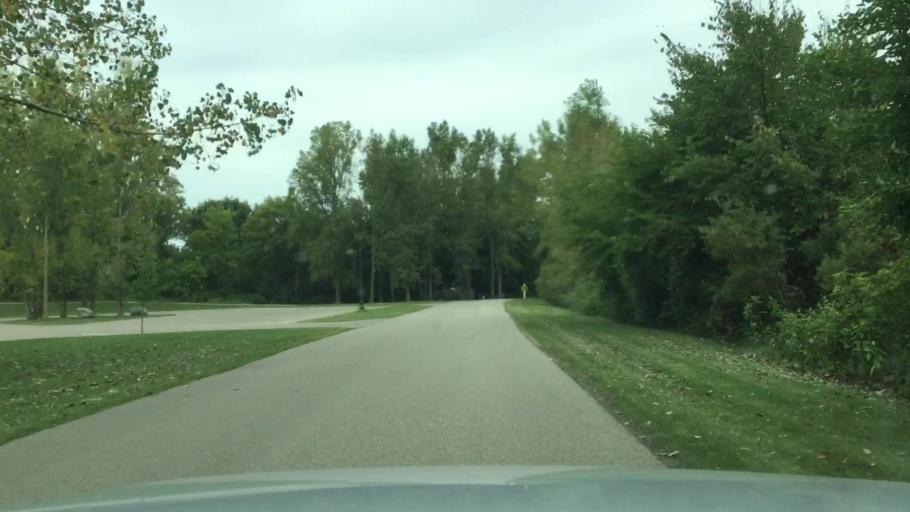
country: US
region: Michigan
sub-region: Shiawassee County
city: Durand
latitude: 42.9528
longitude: -83.9566
